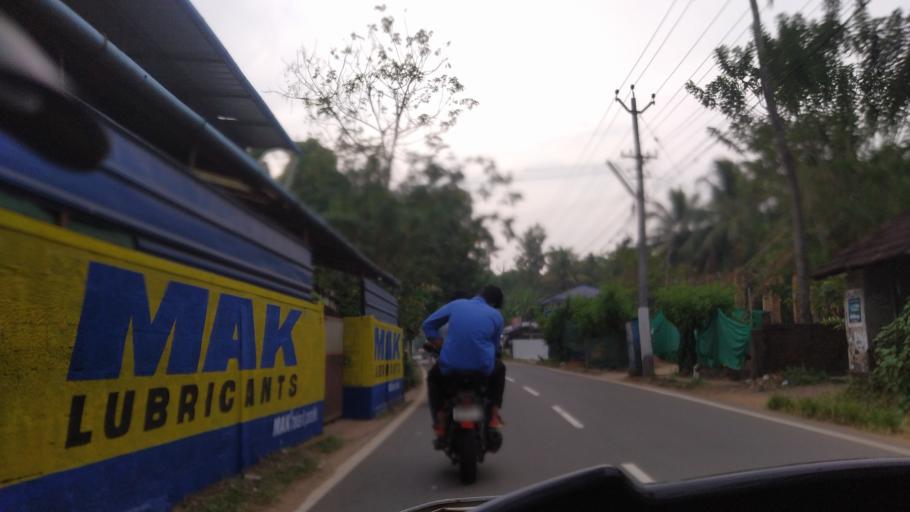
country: IN
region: Kerala
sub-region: Ernakulam
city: Elur
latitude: 10.1499
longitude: 76.2626
